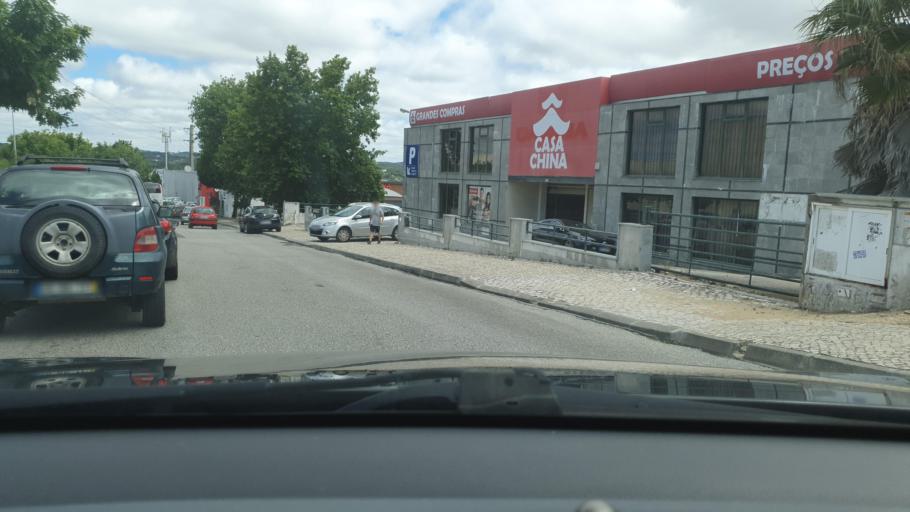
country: PT
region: Lisbon
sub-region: Sintra
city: Cacem
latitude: 38.7671
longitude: -9.2791
